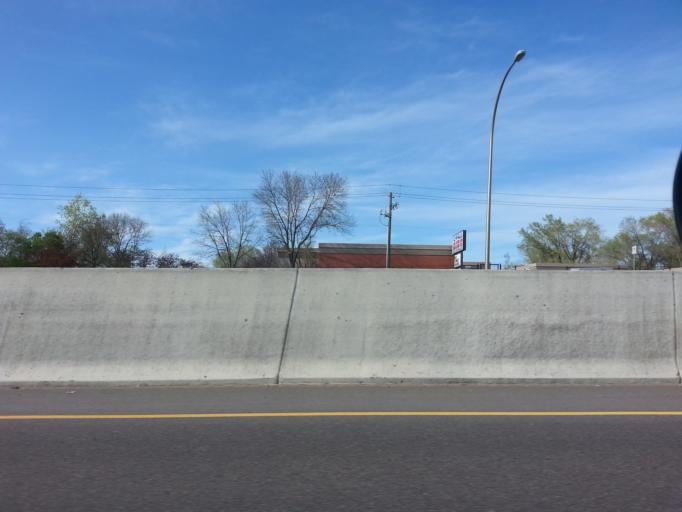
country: US
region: Minnesota
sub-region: Ramsey County
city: Little Canada
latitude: 45.0117
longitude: -93.0505
